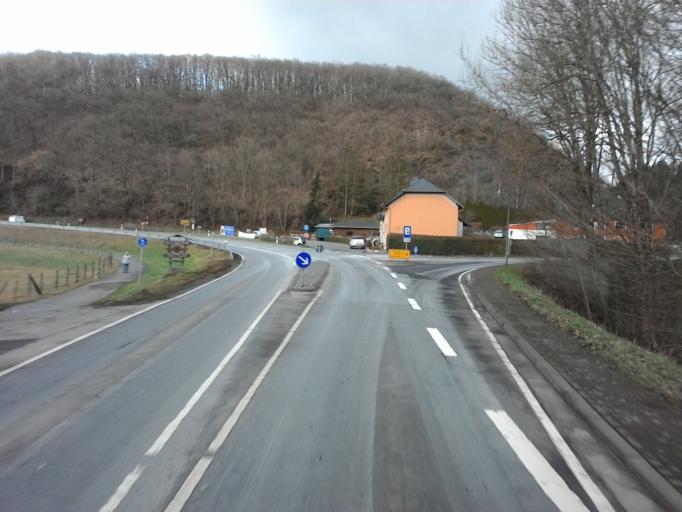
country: DE
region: Rheinland-Pfalz
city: Sinspelt
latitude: 49.9764
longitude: 6.3218
